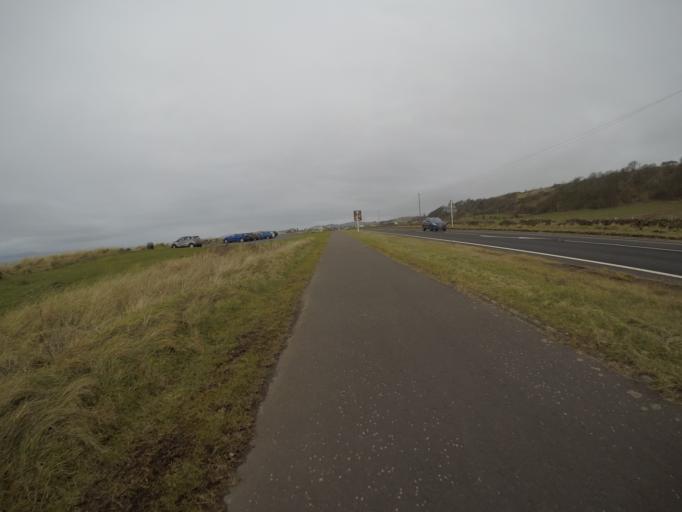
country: GB
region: Scotland
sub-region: North Ayrshire
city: West Kilbride
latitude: 55.6707
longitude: -4.8465
